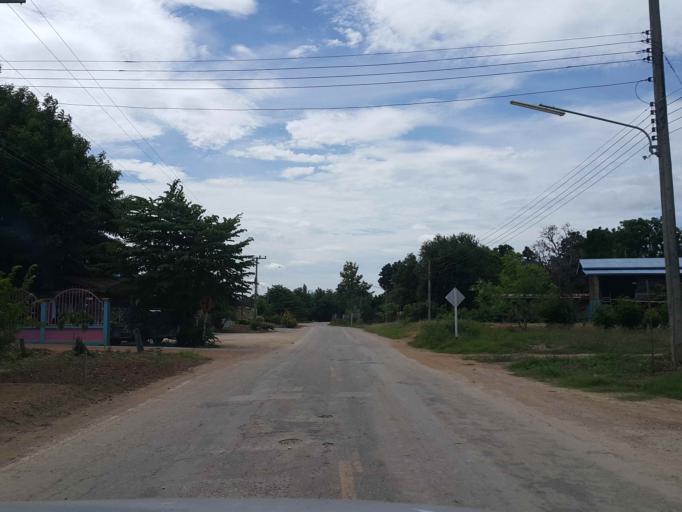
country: TH
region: Sukhothai
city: Ban Dan Lan Hoi
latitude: 17.0755
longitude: 99.4808
